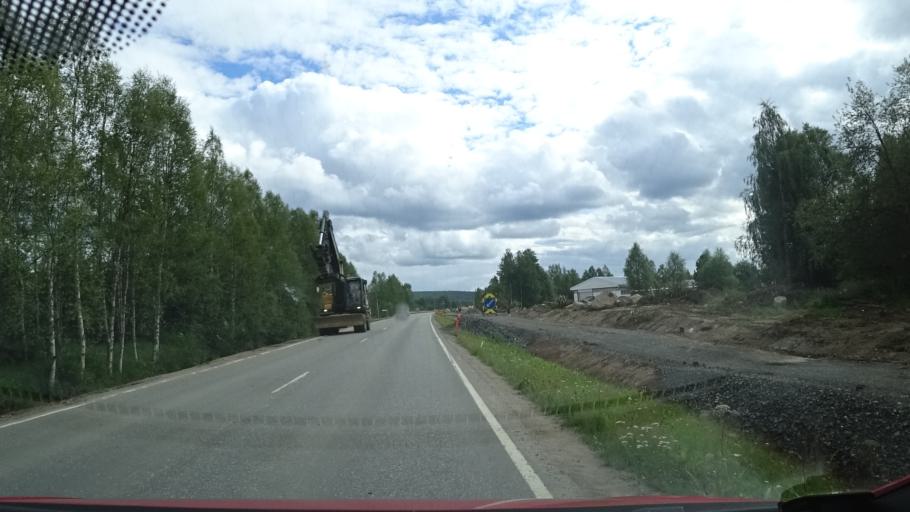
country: FI
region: Lapland
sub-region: Rovaniemi
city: Rovaniemi
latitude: 66.5286
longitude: 25.7399
